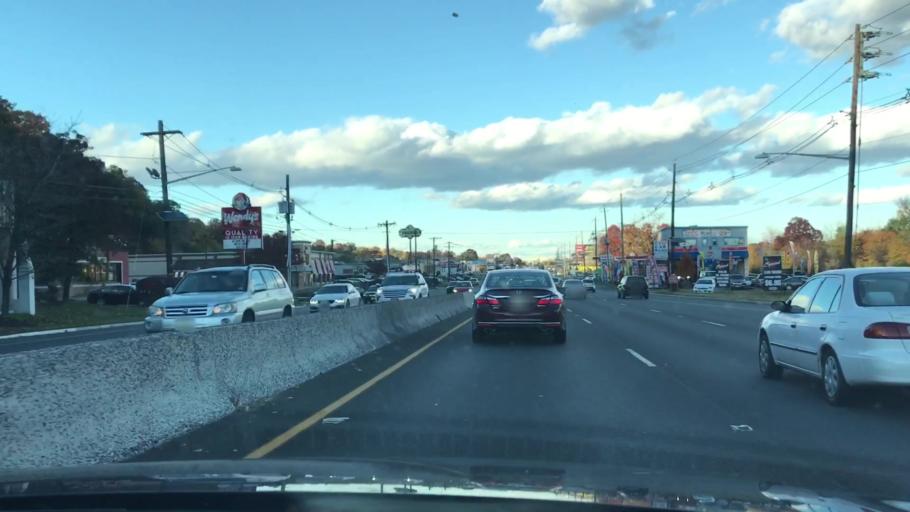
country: US
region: New Jersey
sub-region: Bergen County
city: Hasbrouck Heights
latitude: 40.8475
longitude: -74.0766
